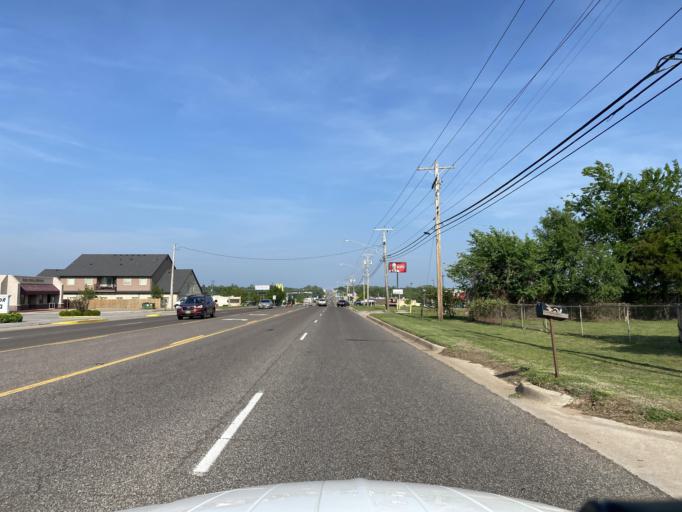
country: US
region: Oklahoma
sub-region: Oklahoma County
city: Spencer
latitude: 35.4930
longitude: -97.3737
